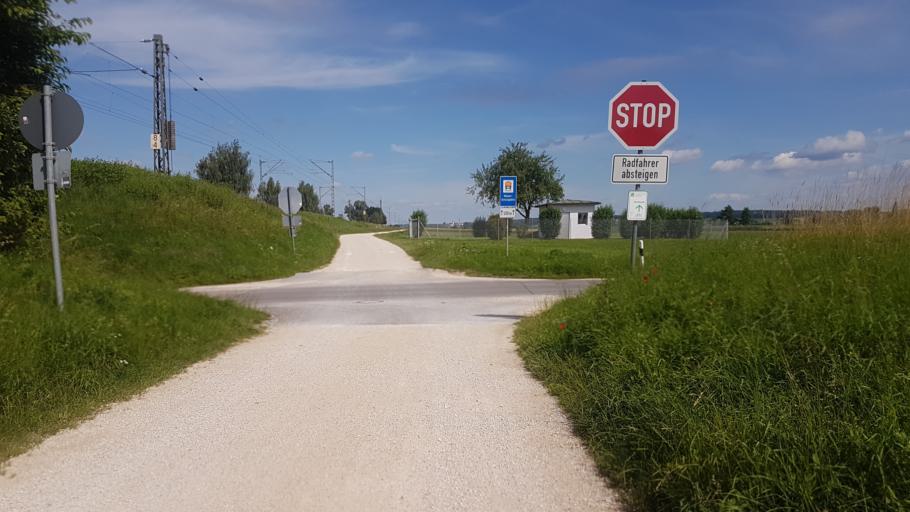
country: DE
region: Bavaria
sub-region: Regierungsbezirk Mittelfranken
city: Markt Berolzheim
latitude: 49.0203
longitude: 10.8507
